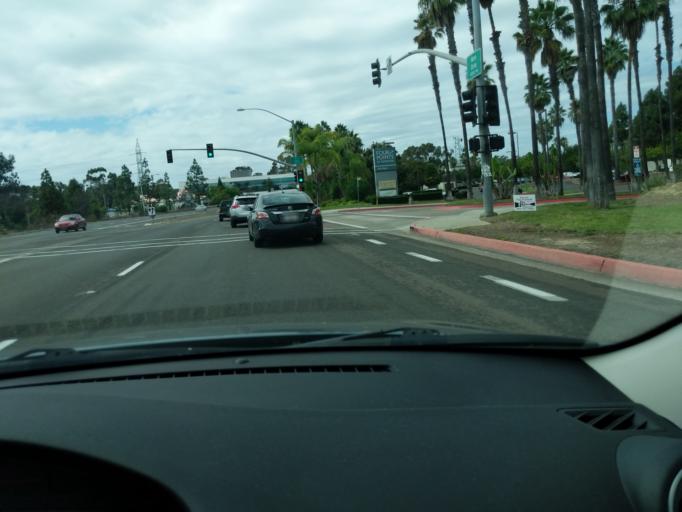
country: US
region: California
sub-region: San Diego County
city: San Diego
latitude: 32.8097
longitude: -117.1482
